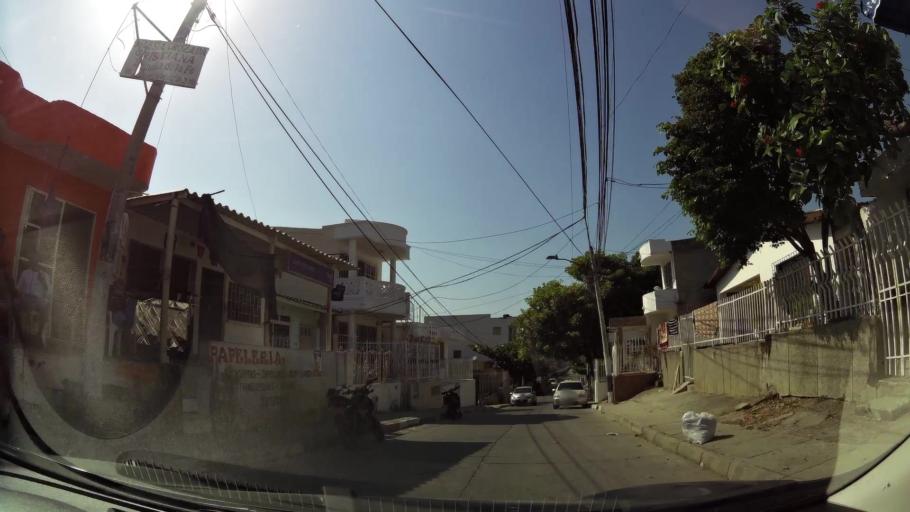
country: CO
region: Bolivar
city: Cartagena
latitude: 10.3986
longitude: -75.4960
